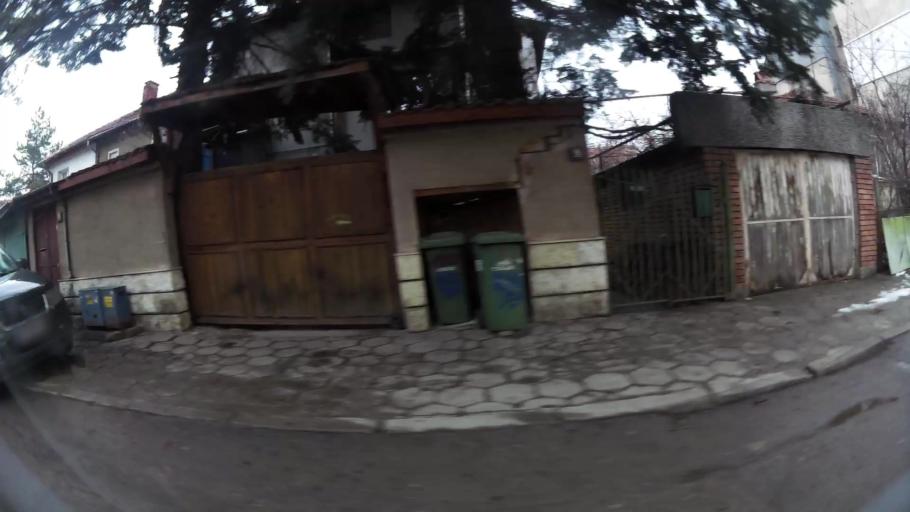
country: BG
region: Sofia-Capital
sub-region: Stolichna Obshtina
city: Sofia
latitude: 42.6685
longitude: 23.2513
